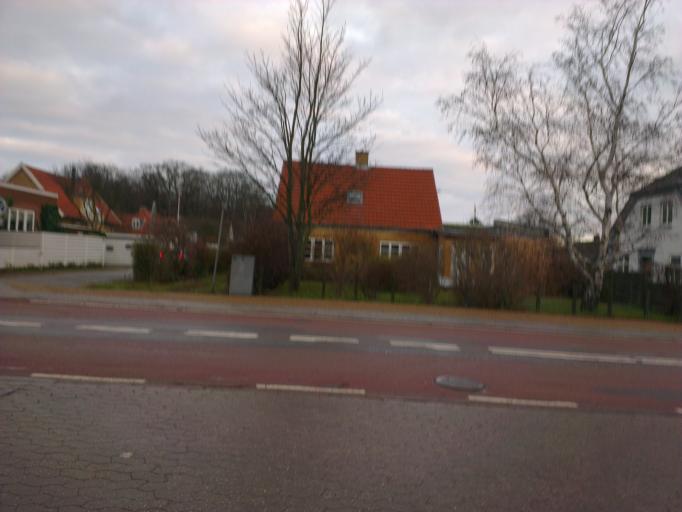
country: DK
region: Capital Region
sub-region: Frederikssund Kommune
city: Jaegerspris
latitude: 55.8552
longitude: 11.9864
